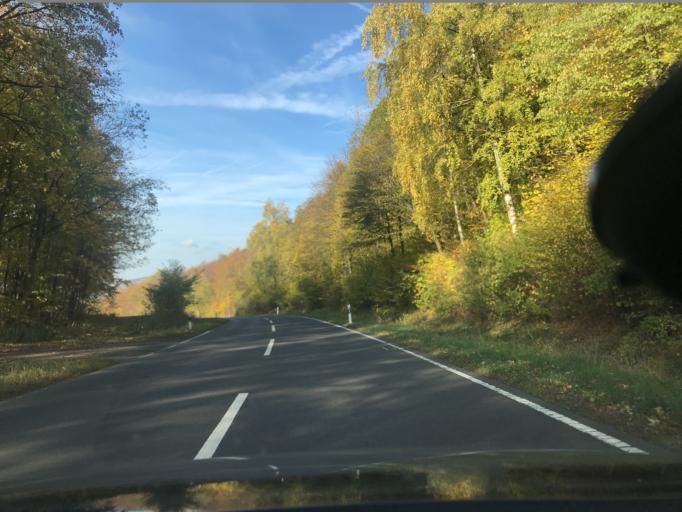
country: DE
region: Hesse
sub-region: Regierungsbezirk Kassel
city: Grossalmerode
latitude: 51.2129
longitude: 9.8276
